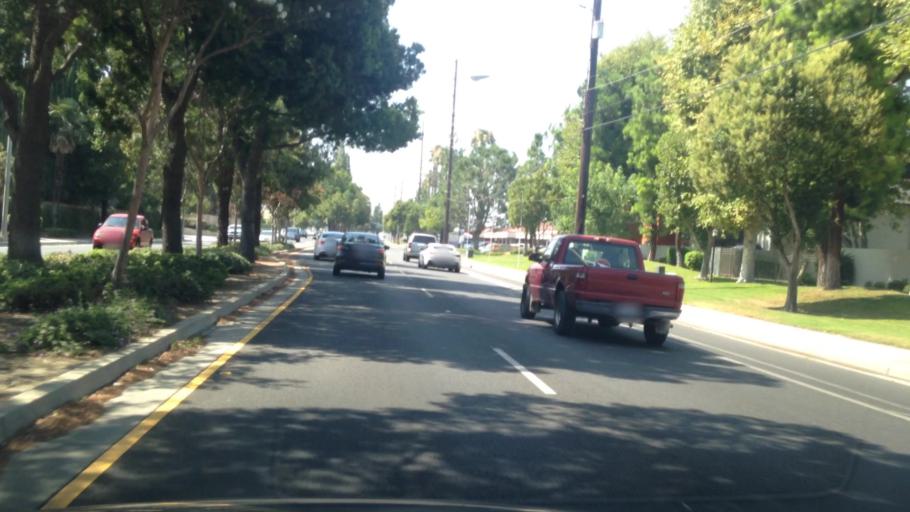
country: US
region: California
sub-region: Riverside County
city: Home Gardens
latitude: 33.9129
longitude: -117.4839
